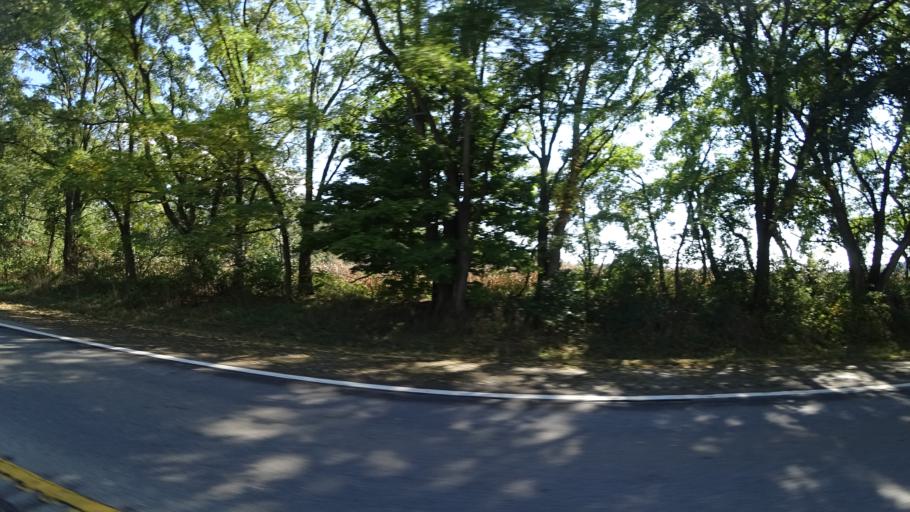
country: US
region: Michigan
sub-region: Calhoun County
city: Homer
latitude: 42.1535
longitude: -84.7855
